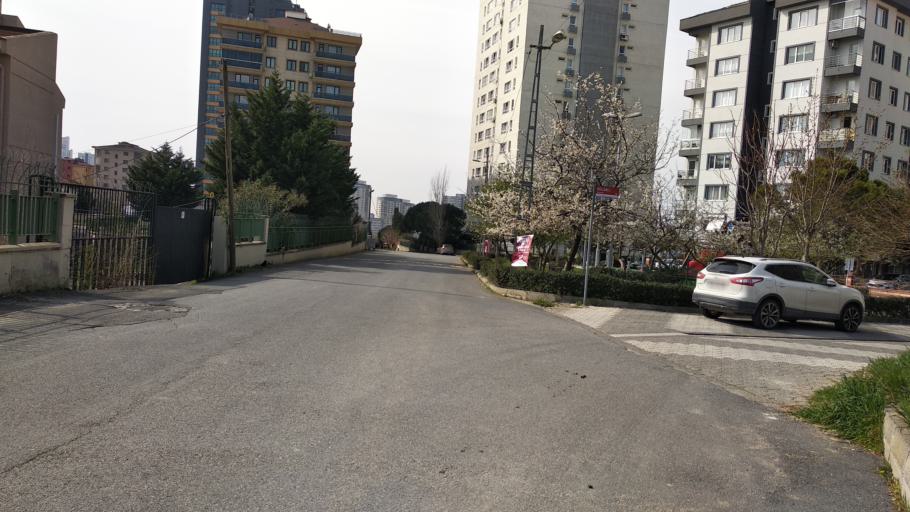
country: TR
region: Istanbul
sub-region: Atasehir
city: Atasehir
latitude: 40.9857
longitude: 29.1161
